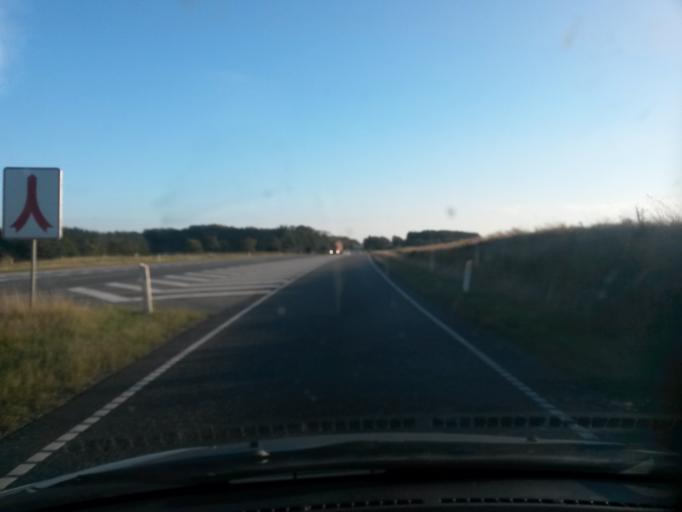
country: DK
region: Central Jutland
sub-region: Silkeborg Kommune
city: Kjellerup
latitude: 56.2982
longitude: 9.3220
